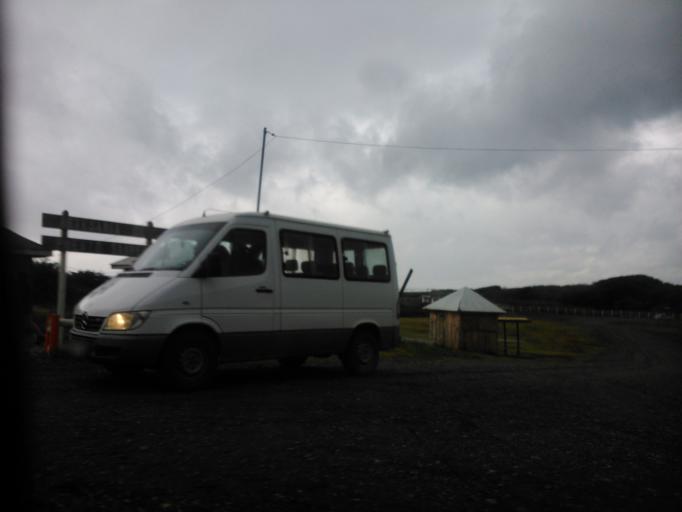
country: CL
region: Araucania
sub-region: Provincia de Cautin
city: Carahue
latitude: -38.8130
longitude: -73.4003
